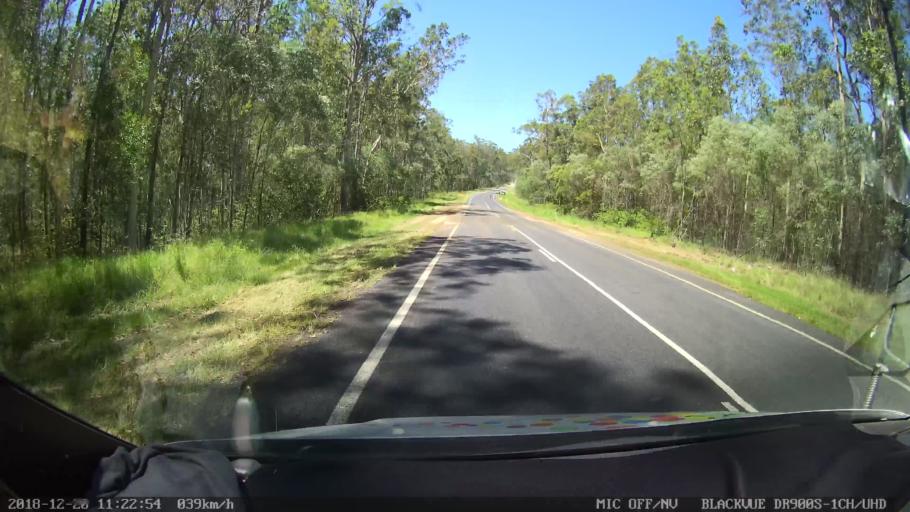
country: AU
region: New South Wales
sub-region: Richmond Valley
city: Casino
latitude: -29.0626
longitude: 153.0048
